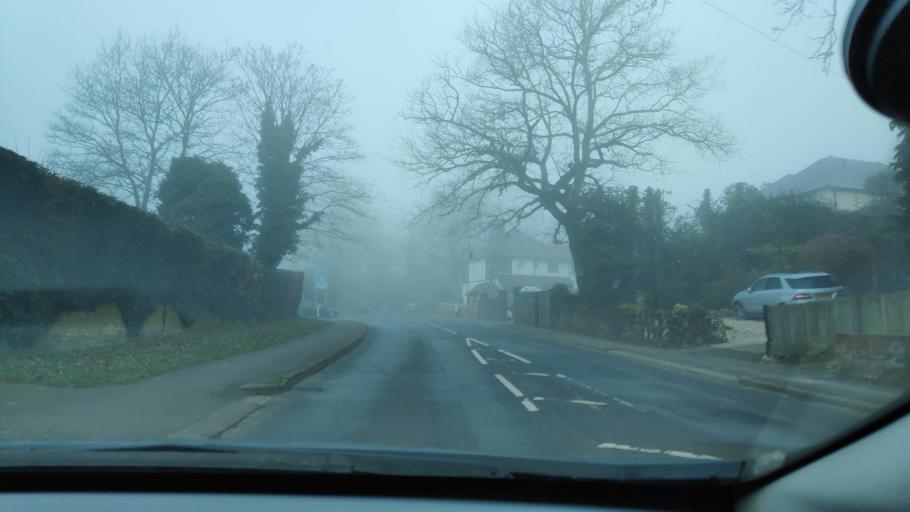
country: GB
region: England
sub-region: Hampshire
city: Farnborough
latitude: 51.2869
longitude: -0.7435
